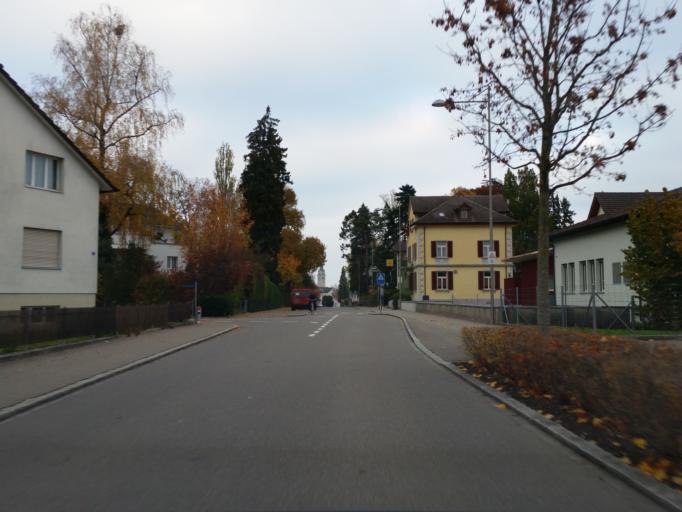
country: CH
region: Thurgau
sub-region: Arbon District
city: Salmsach
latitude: 47.5623
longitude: 9.3710
